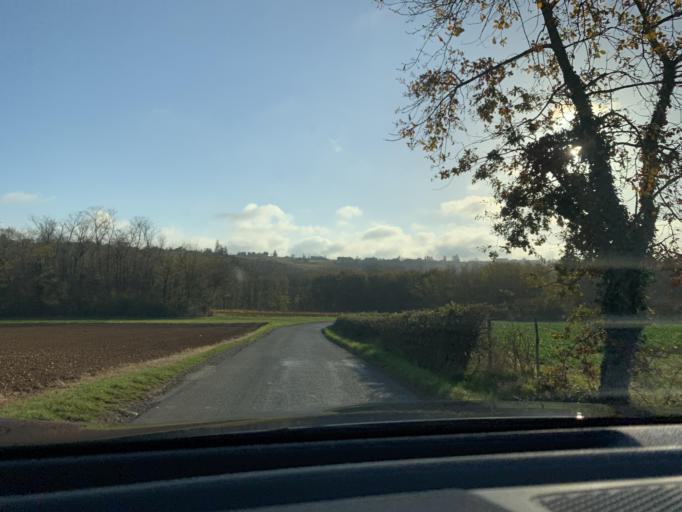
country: FR
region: Rhone-Alpes
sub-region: Departement du Rhone
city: Pommiers
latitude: 45.9472
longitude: 4.6742
